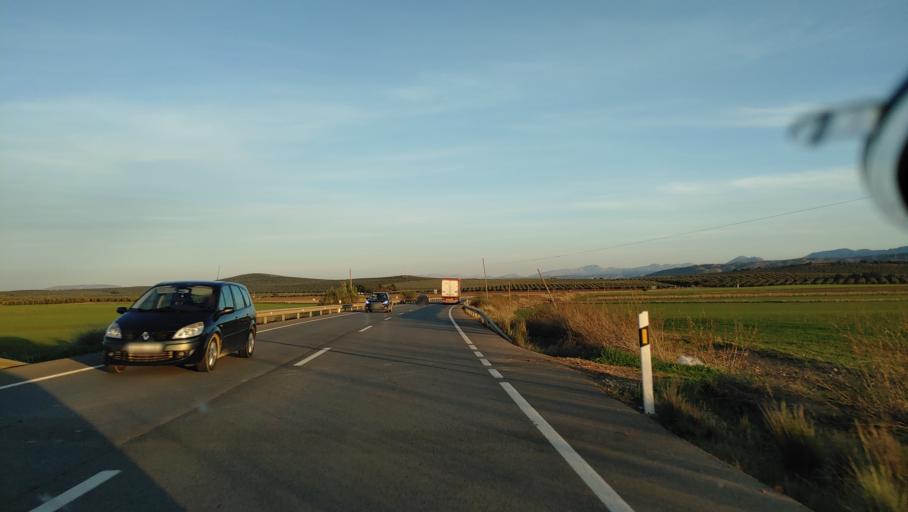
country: ES
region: Andalusia
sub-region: Provincia de Malaga
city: Humilladero
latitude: 37.0630
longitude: -4.7026
